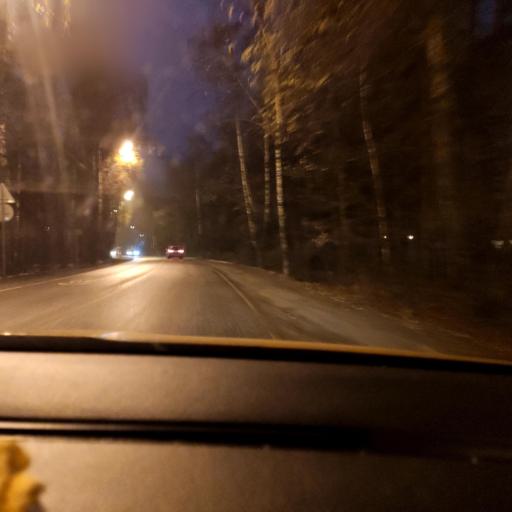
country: RU
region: Moskovskaya
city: Lesnoy Gorodok
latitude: 55.6352
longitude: 37.2061
